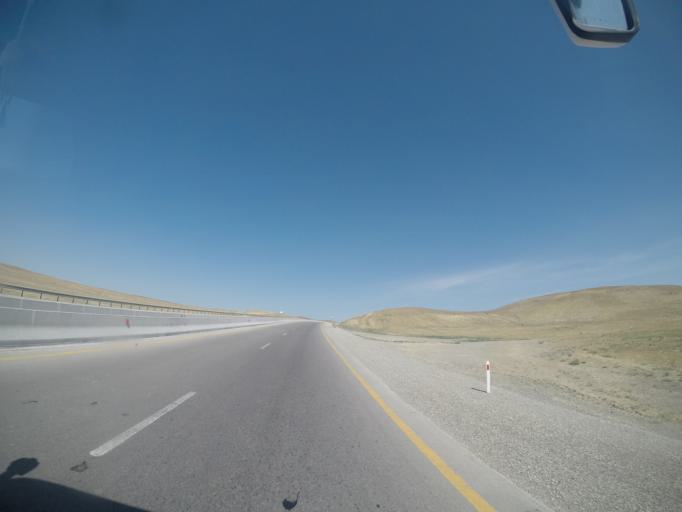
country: AZ
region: Sumqayit
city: Haci Zeynalabdin
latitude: 40.4769
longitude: 49.4499
